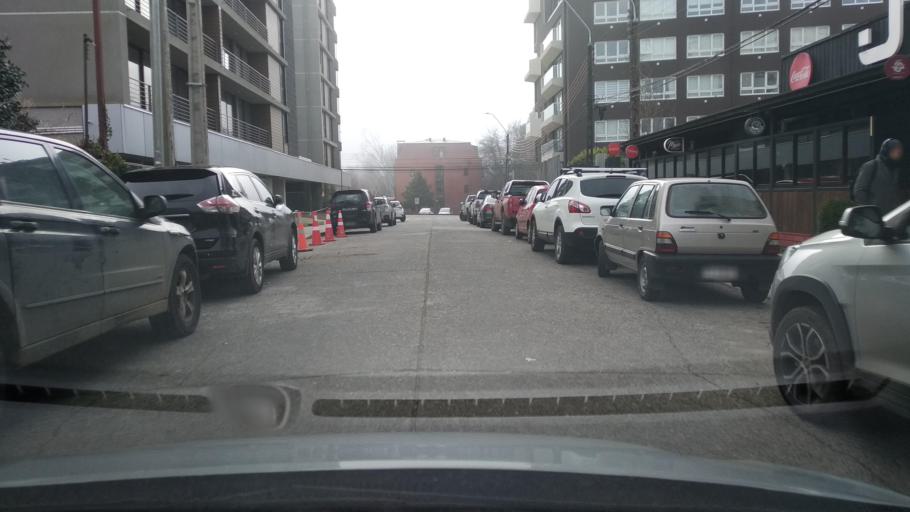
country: CL
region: Los Rios
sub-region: Provincia de Valdivia
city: Valdivia
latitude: -39.8104
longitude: -73.2532
